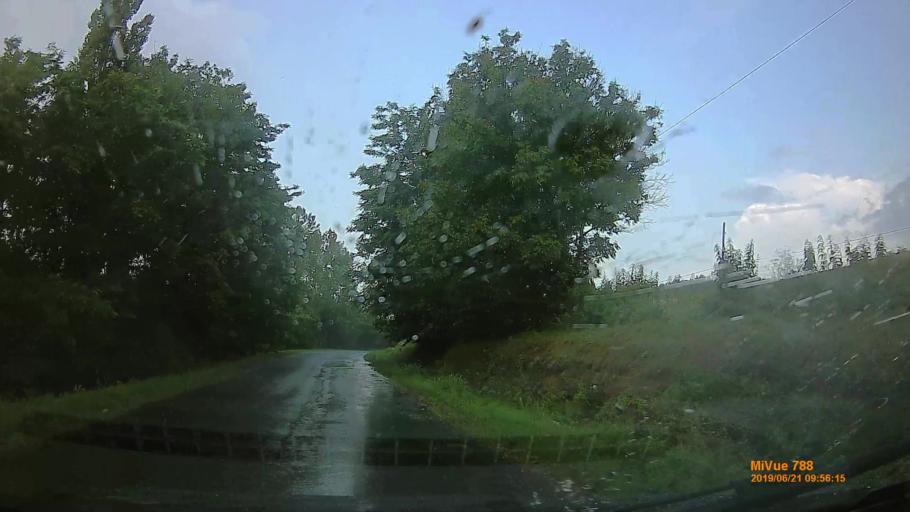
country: HU
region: Baranya
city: Buekkoesd
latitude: 46.2262
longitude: 17.9820
